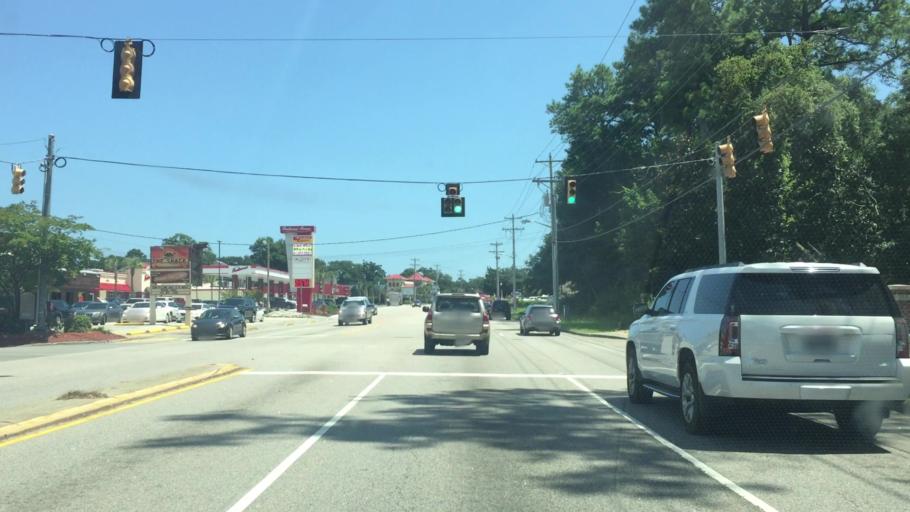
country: US
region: South Carolina
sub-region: Horry County
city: North Myrtle Beach
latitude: 33.8426
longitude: -78.6484
